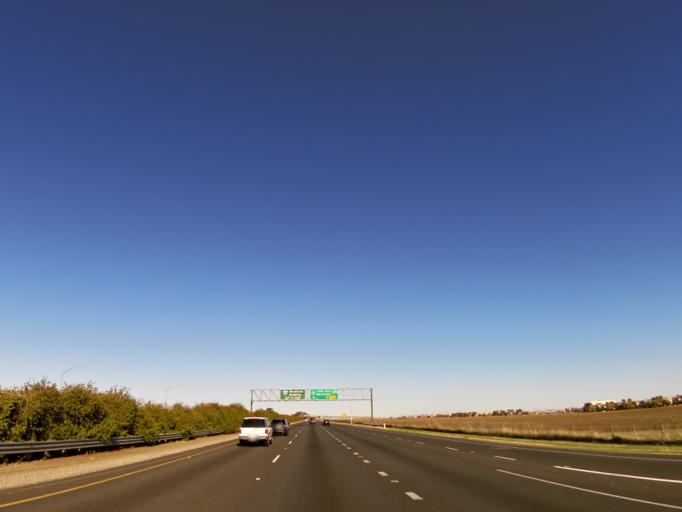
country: US
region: California
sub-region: Yolo County
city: West Sacramento
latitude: 38.6580
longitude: -121.5339
